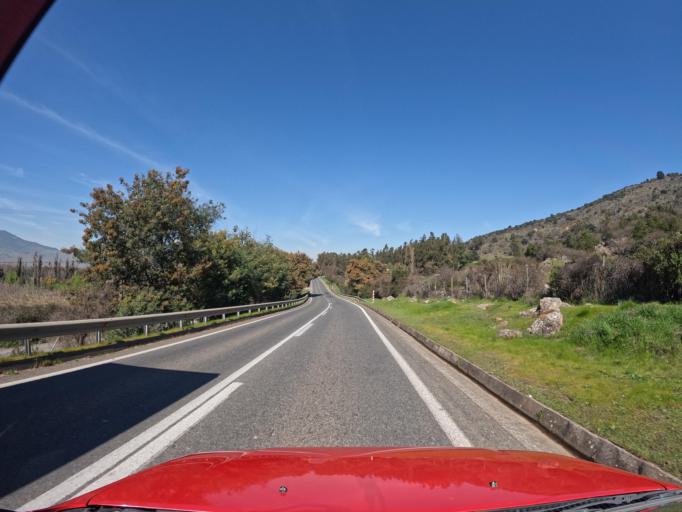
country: CL
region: Maule
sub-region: Provincia de Curico
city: Rauco
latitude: -35.0679
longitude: -71.6244
